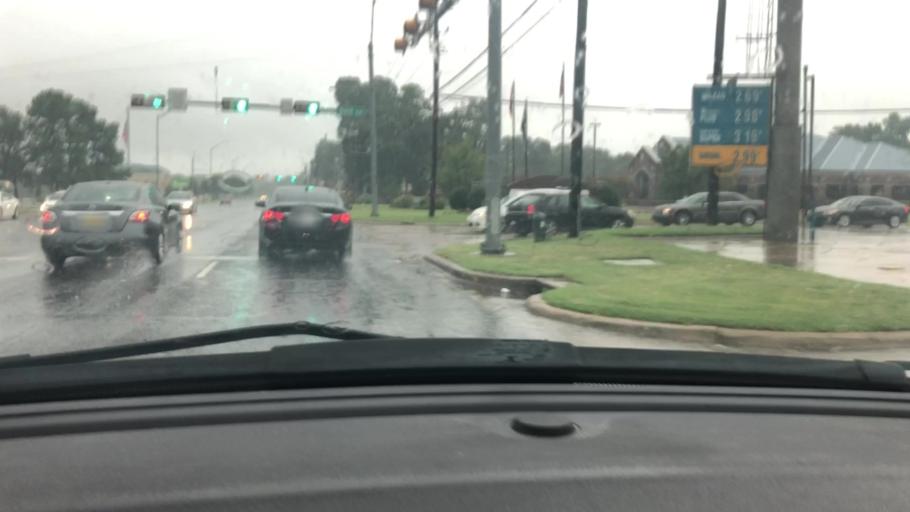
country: US
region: Texas
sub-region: Bowie County
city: Wake Village
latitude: 33.4545
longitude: -94.0844
